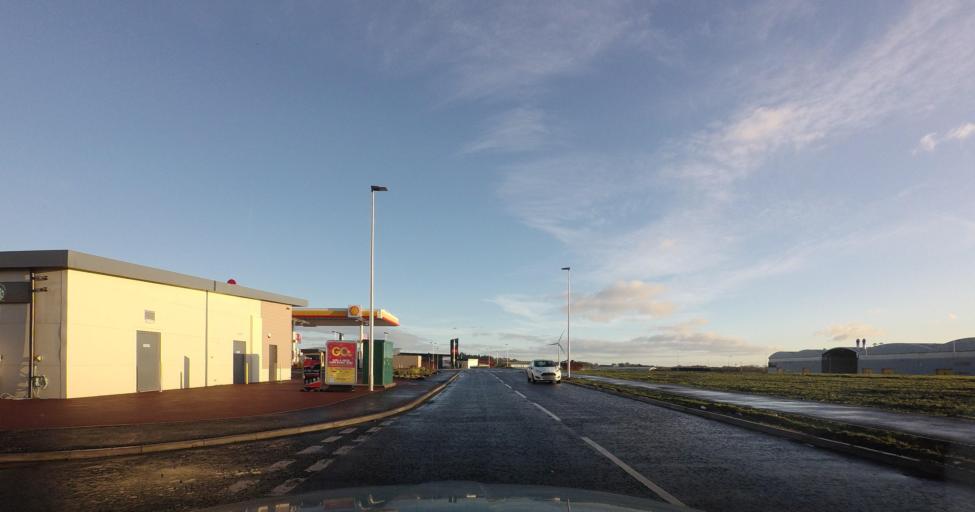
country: GB
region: Scotland
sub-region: West Lothian
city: Armadale
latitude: 55.8684
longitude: -3.7030
